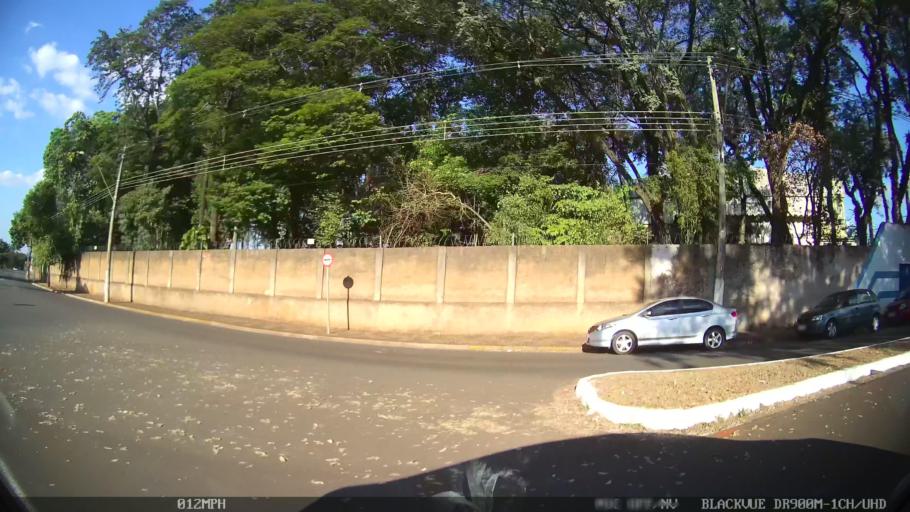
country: BR
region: Sao Paulo
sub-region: Santa Barbara D'Oeste
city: Santa Barbara d'Oeste
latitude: -22.7519
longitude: -47.4256
